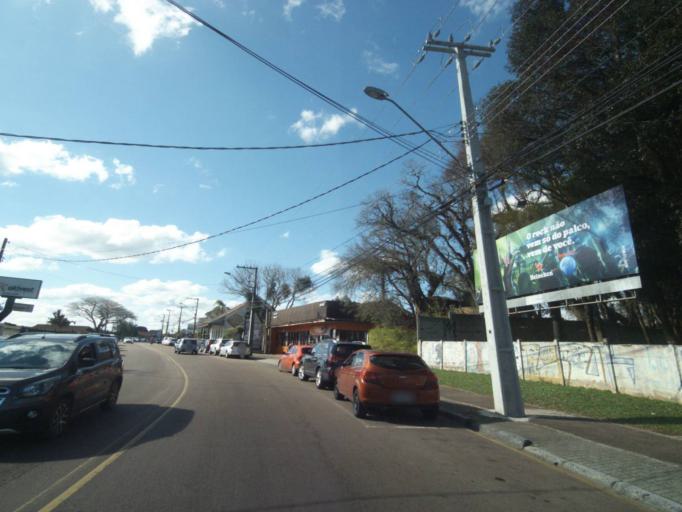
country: BR
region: Parana
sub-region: Curitiba
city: Curitiba
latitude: -25.3875
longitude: -49.2609
